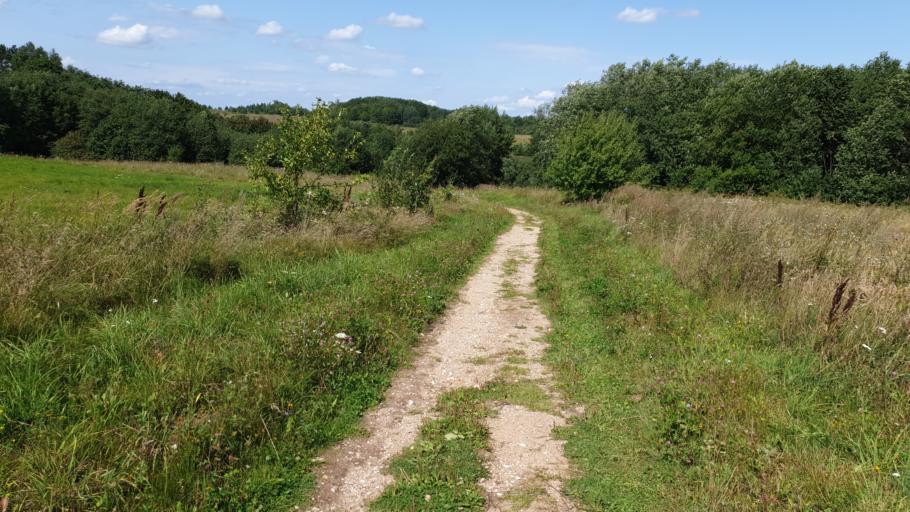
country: LT
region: Vilnius County
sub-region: Vilniaus Rajonas
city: Vievis
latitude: 54.8224
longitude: 24.9457
